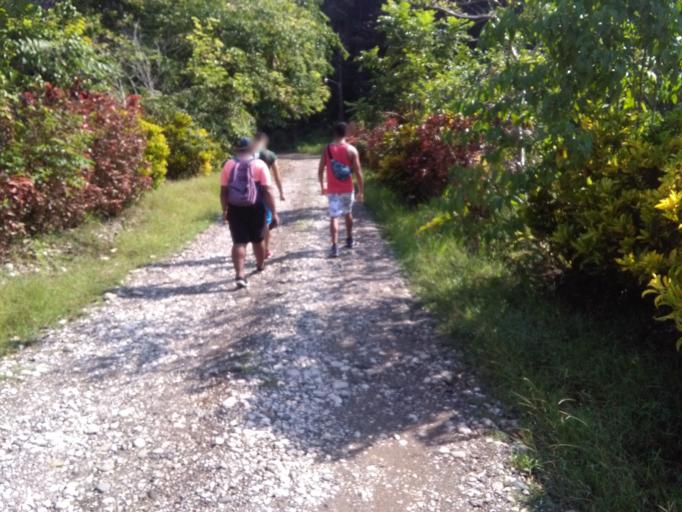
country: CR
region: Puntarenas
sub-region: Canton de Golfito
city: Golfito
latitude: 8.6497
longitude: -83.1770
